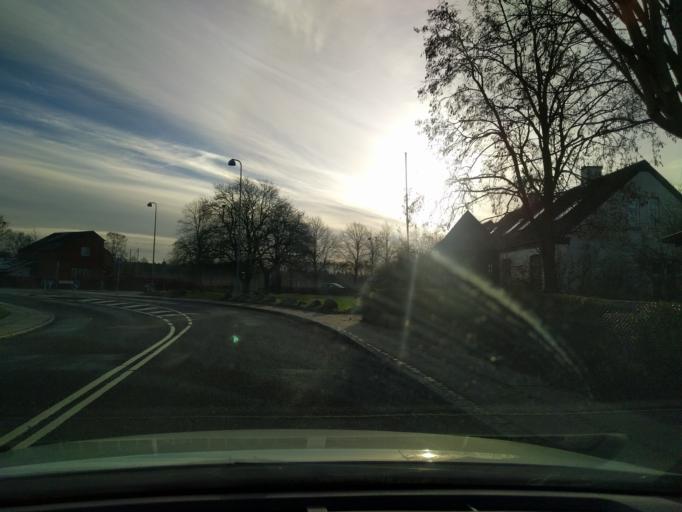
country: DK
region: South Denmark
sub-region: Odense Kommune
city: Neder Holluf
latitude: 55.3570
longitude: 10.4931
